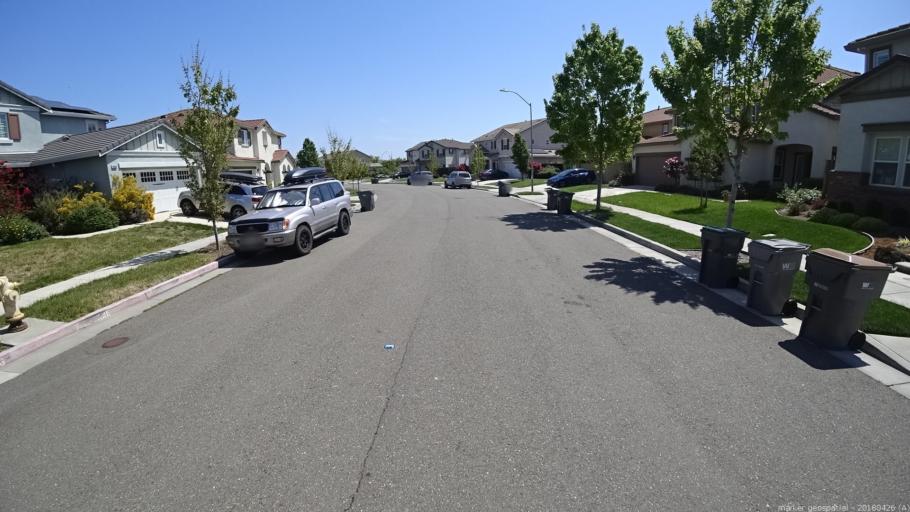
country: US
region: California
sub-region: Yolo County
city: West Sacramento
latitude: 38.5329
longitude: -121.5799
